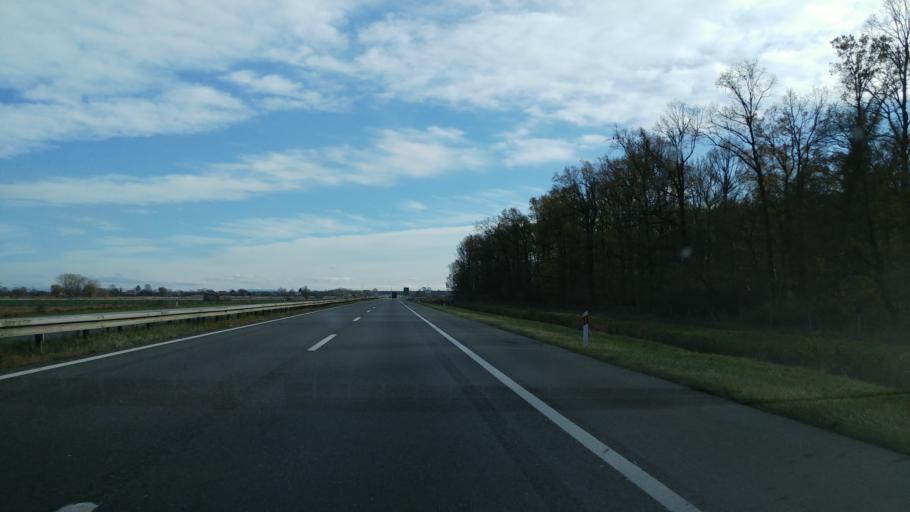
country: HR
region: Sisacko-Moslavacka
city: Repusnica
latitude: 45.4701
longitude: 16.7418
